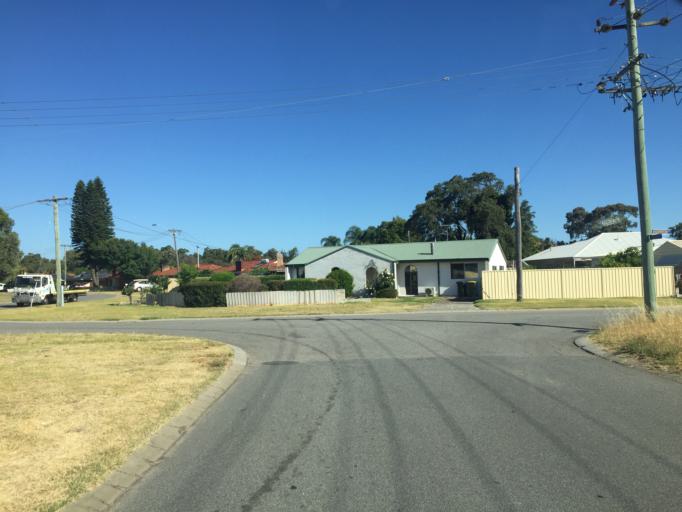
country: AU
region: Western Australia
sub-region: Canning
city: East Cannington
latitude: -32.0131
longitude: 115.9669
